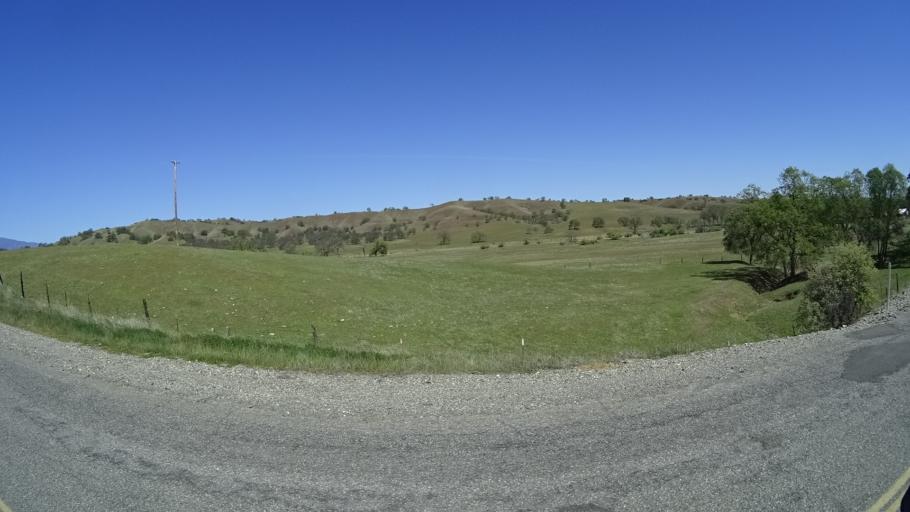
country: US
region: California
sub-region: Tehama County
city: Rancho Tehama Reserve
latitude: 39.7867
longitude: -122.4625
